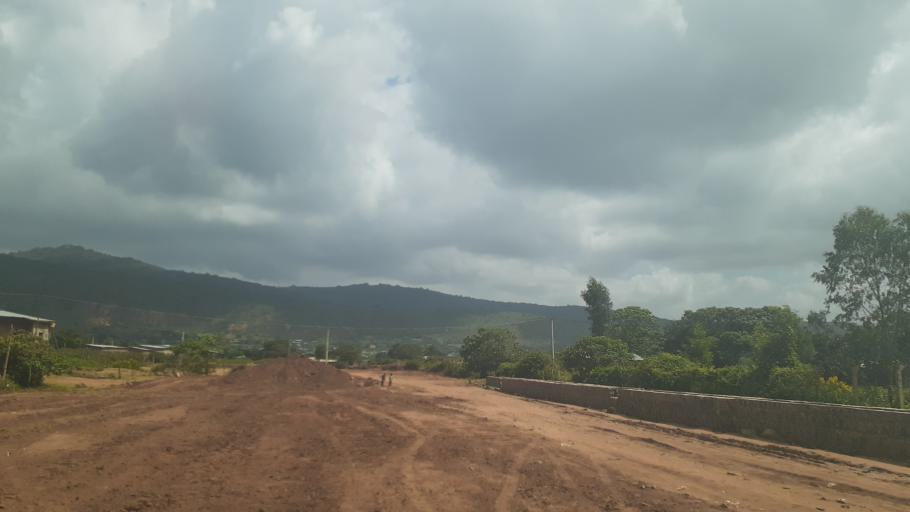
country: ET
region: Oromiya
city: Yabelo
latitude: 4.8945
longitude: 38.0840
